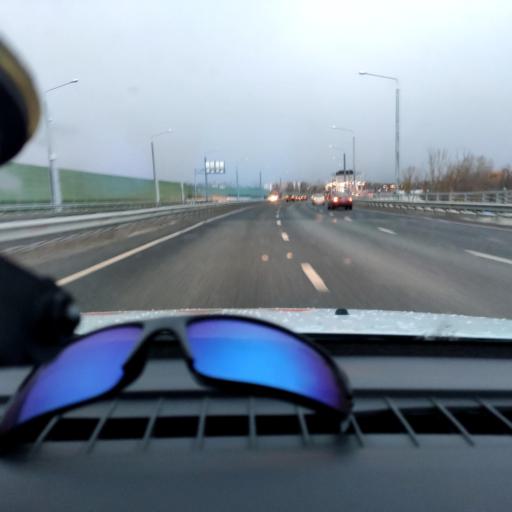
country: RU
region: Samara
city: Samara
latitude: 53.1657
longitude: 50.0856
